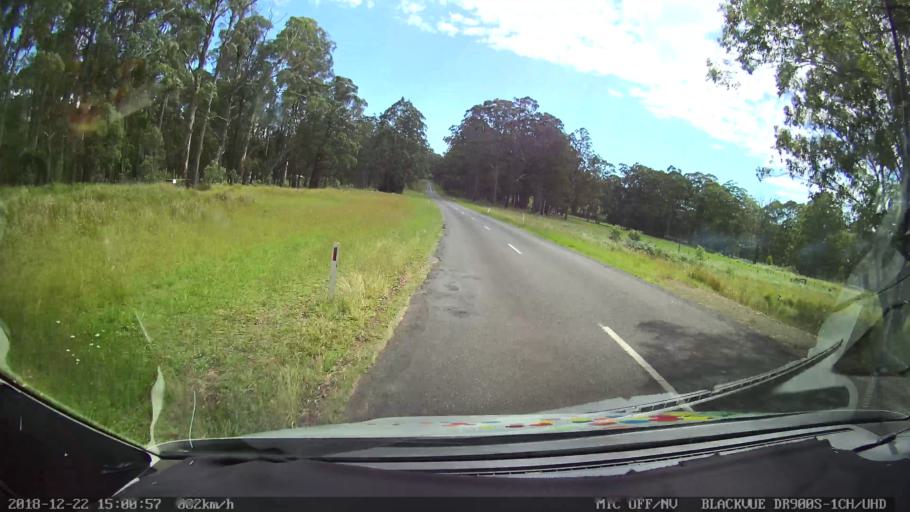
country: AU
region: New South Wales
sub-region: Bellingen
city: Dorrigo
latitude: -30.2500
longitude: 152.4632
